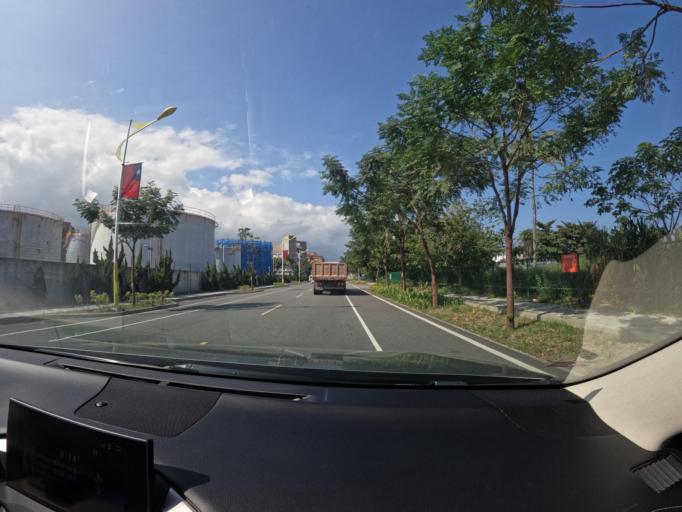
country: TW
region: Taiwan
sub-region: Hualien
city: Hualian
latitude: 23.9979
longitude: 121.6331
